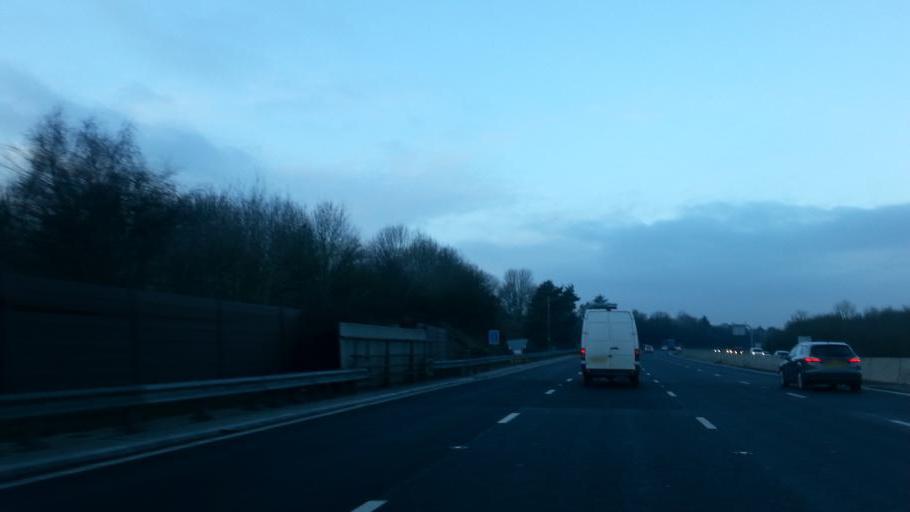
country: GB
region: England
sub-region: Worcestershire
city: Droitwich
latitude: 52.2578
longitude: -2.1361
